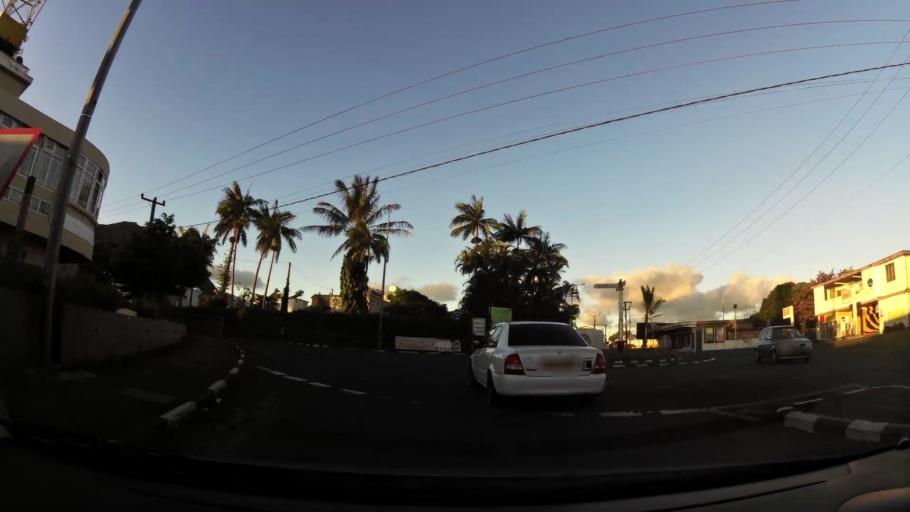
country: MU
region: Moka
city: Moka
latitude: -20.2261
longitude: 57.5068
